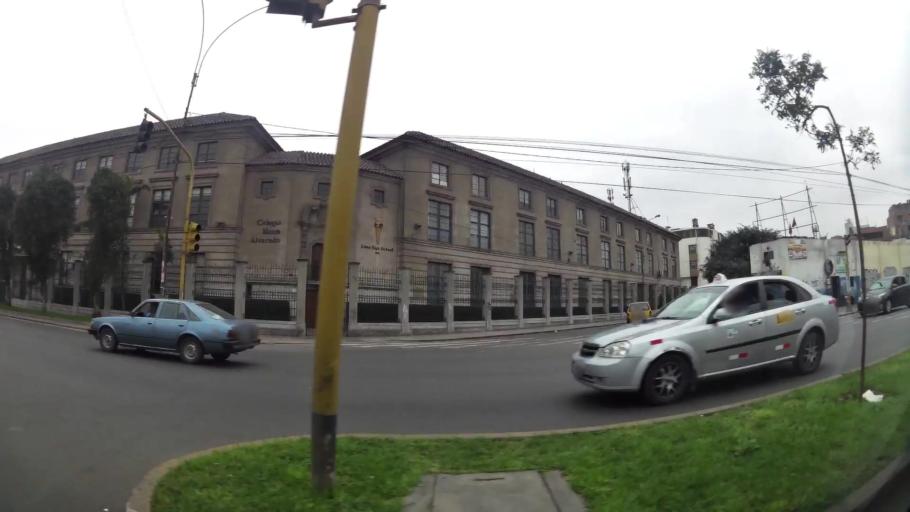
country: PE
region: Lima
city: Lima
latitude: -12.0651
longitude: -77.0436
